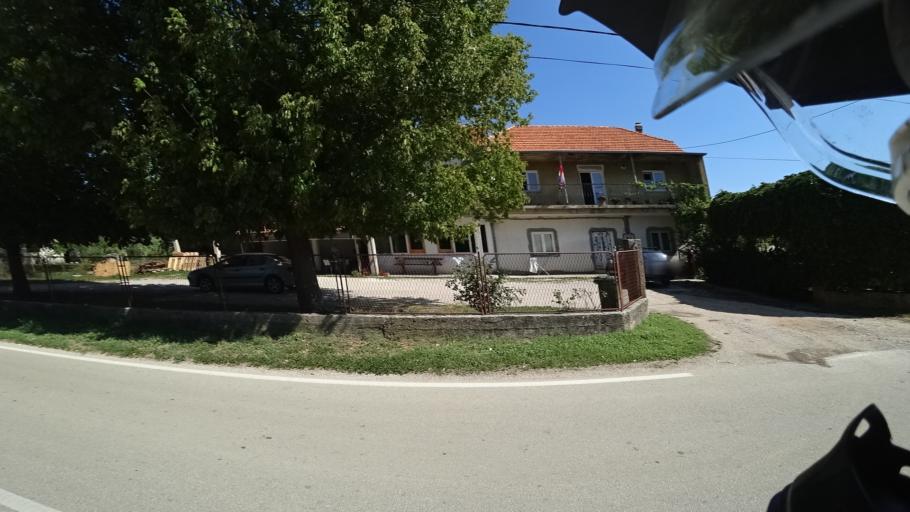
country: HR
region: Sibensko-Kniniska
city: Drnis
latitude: 43.8578
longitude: 16.2284
